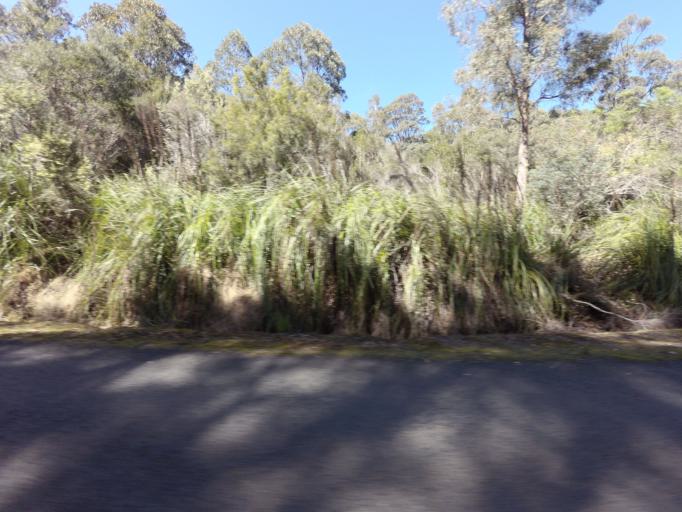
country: AU
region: Tasmania
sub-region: Derwent Valley
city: New Norfolk
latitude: -42.7684
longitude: 146.5825
